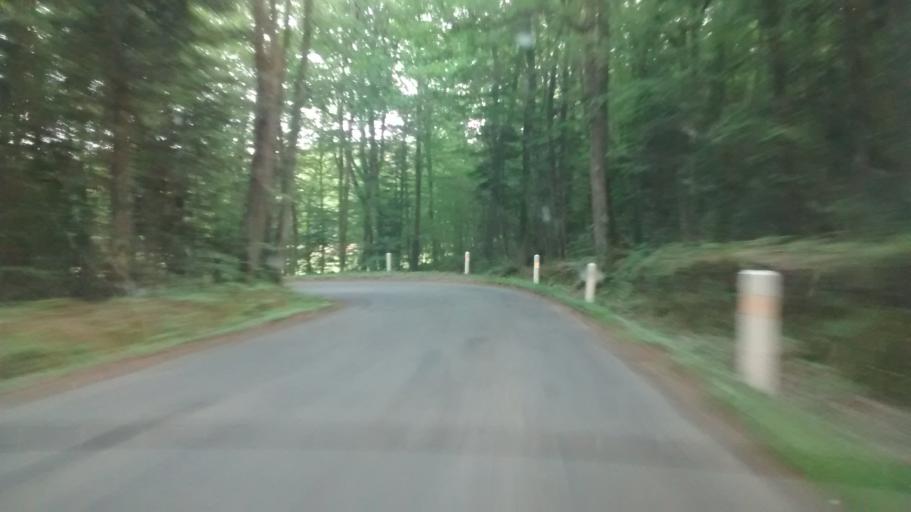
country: FR
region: Brittany
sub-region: Departement d'Ille-et-Vilaine
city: Paimpont
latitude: 47.9975
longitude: -2.1461
